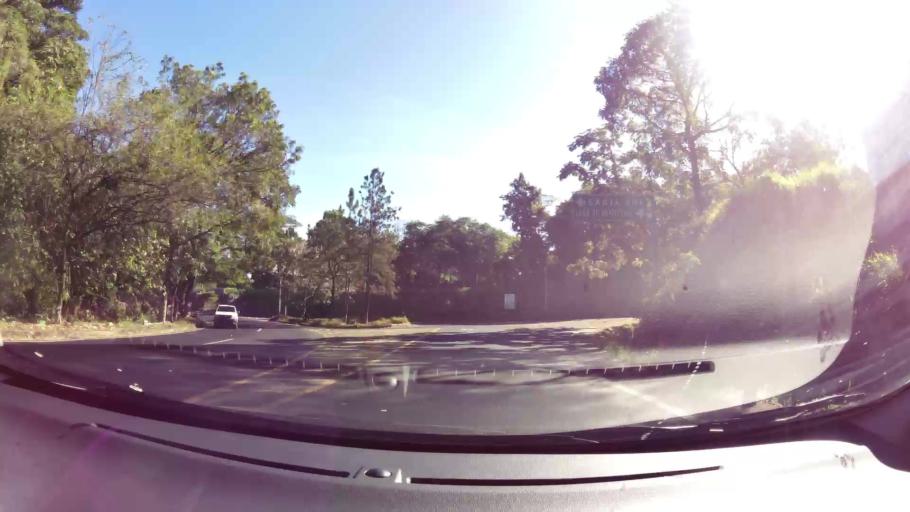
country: SV
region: Santa Ana
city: Santa Ana
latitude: 13.9535
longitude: -89.5689
